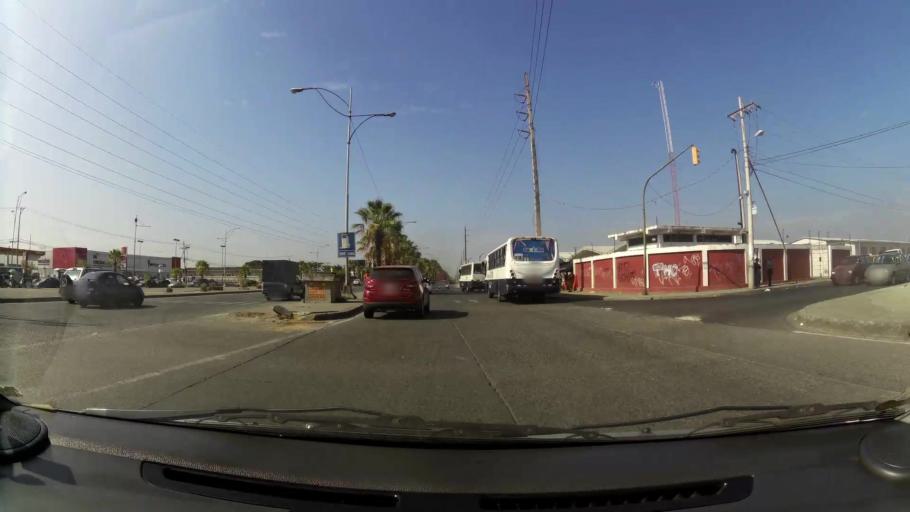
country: EC
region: Guayas
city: Eloy Alfaro
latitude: -2.0920
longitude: -79.9130
